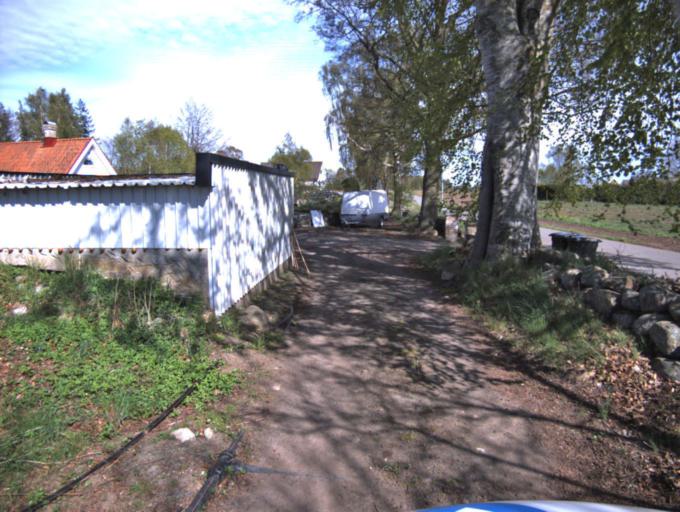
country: SE
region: Skane
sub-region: Kristianstads Kommun
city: Onnestad
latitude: 55.9357
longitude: 14.0004
